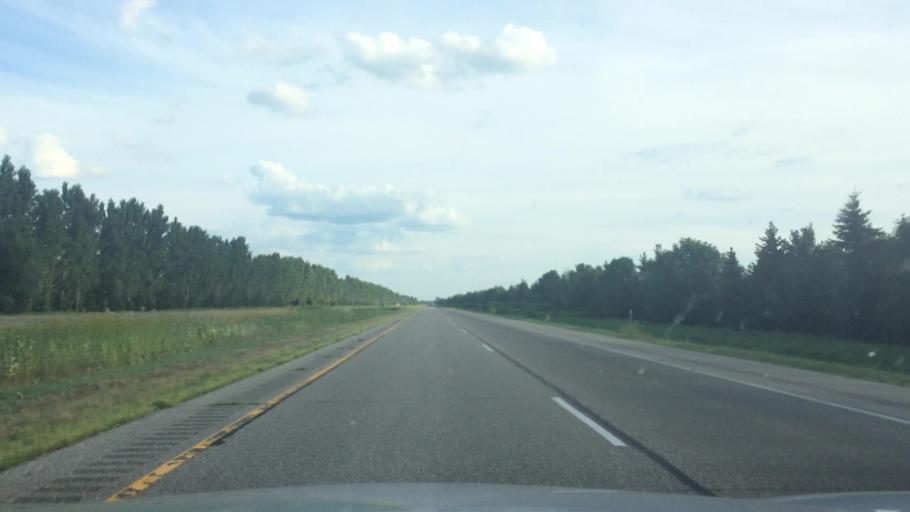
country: US
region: Wisconsin
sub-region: Portage County
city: Plover
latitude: 44.3580
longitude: -89.5211
